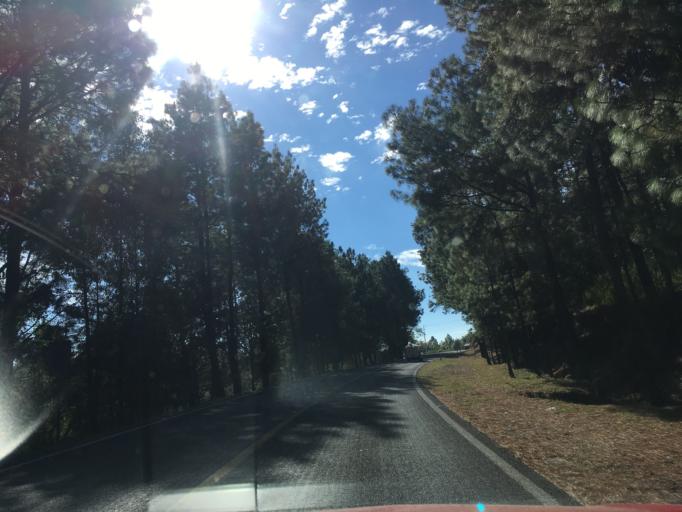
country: MX
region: Michoacan
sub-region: Hidalgo
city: Tierras Coloradas (San Pedro)
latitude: 19.7336
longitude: -100.7584
